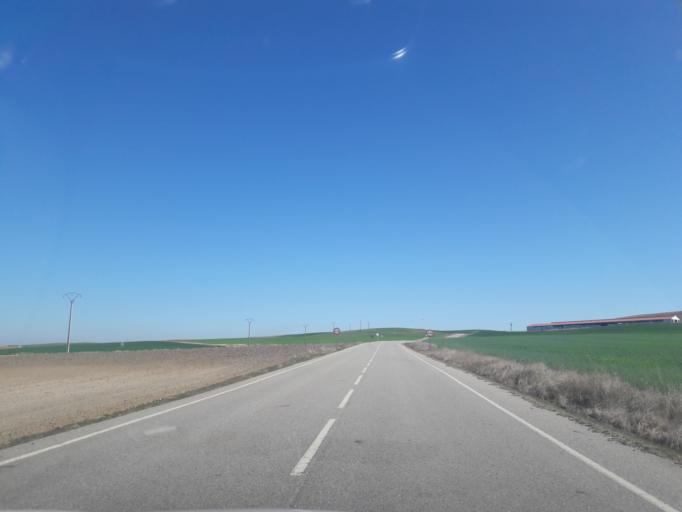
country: ES
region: Castille and Leon
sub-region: Provincia de Salamanca
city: Salmoral
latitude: 40.8099
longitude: -5.2176
